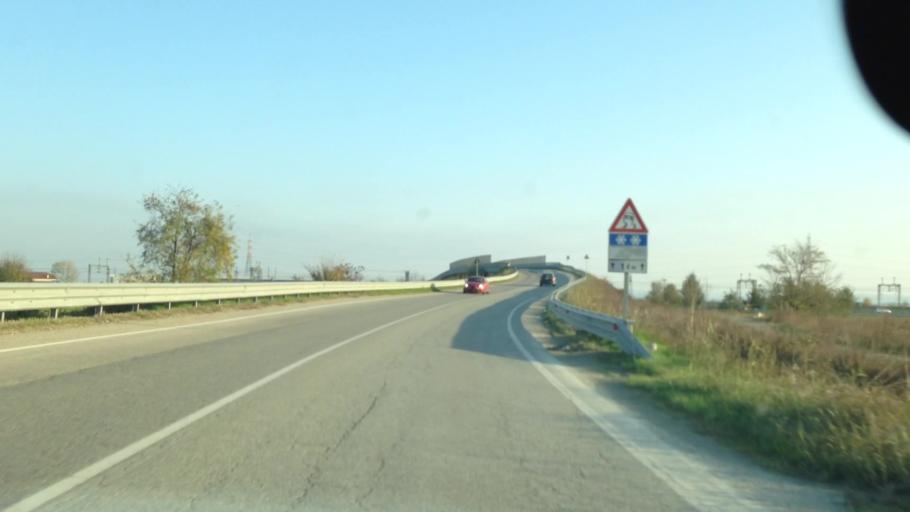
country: IT
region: Piedmont
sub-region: Provincia di Vercelli
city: Cigliano
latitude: 45.2975
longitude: 8.0423
